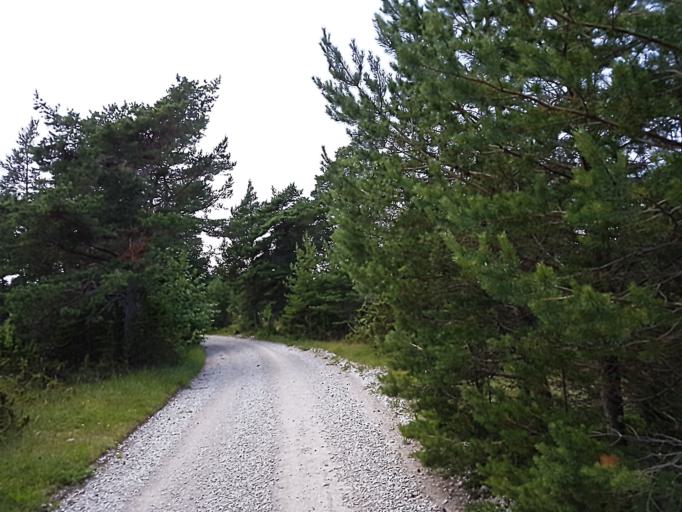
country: SE
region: Gotland
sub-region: Gotland
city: Visby
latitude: 57.6140
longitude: 18.3509
